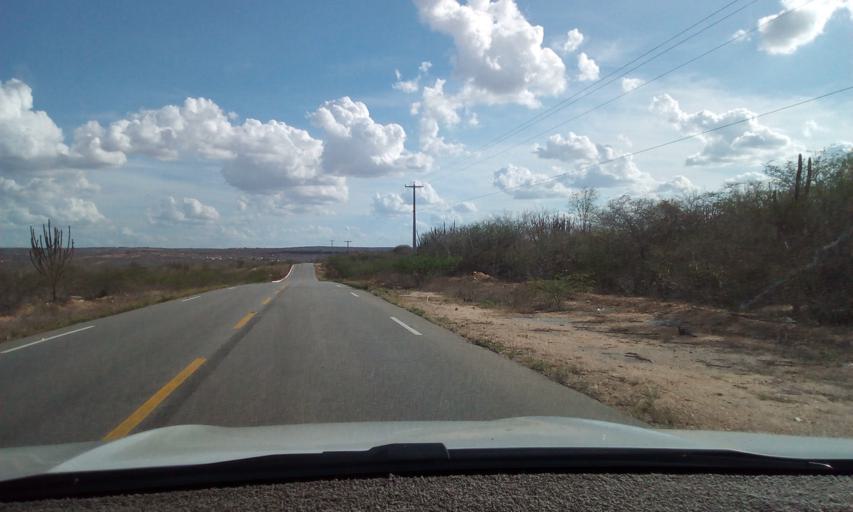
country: BR
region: Paraiba
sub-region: Soledade
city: Soledade
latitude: -6.8385
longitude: -36.4070
